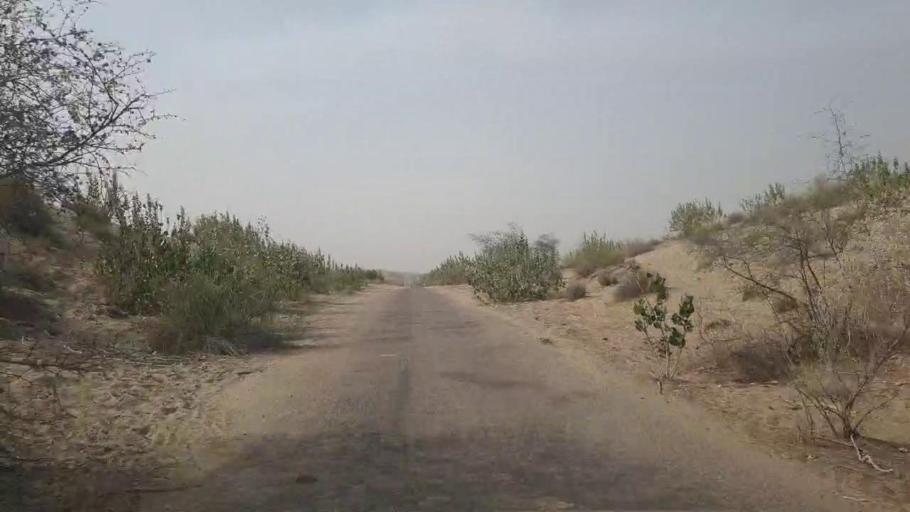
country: PK
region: Sindh
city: Chor
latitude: 25.5996
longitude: 69.9420
